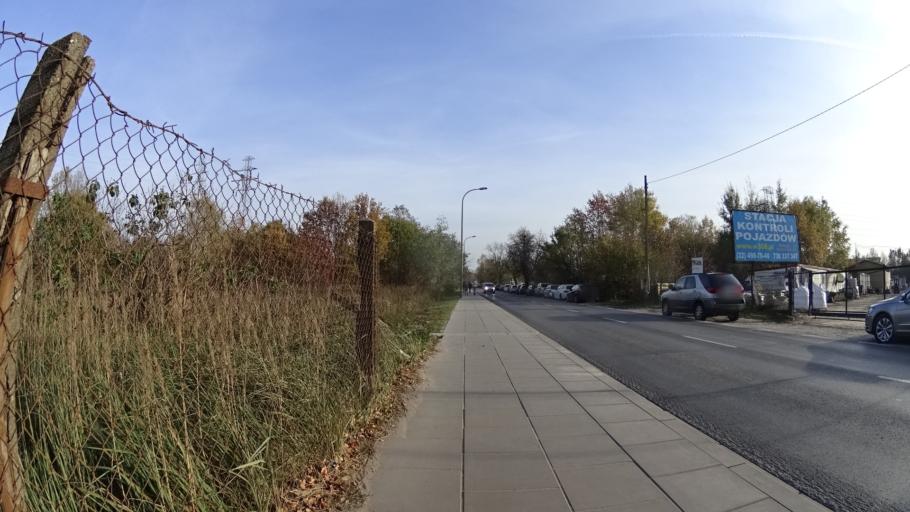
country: PL
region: Masovian Voivodeship
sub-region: Powiat warszawski zachodni
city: Lomianki
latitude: 52.2967
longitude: 20.8906
